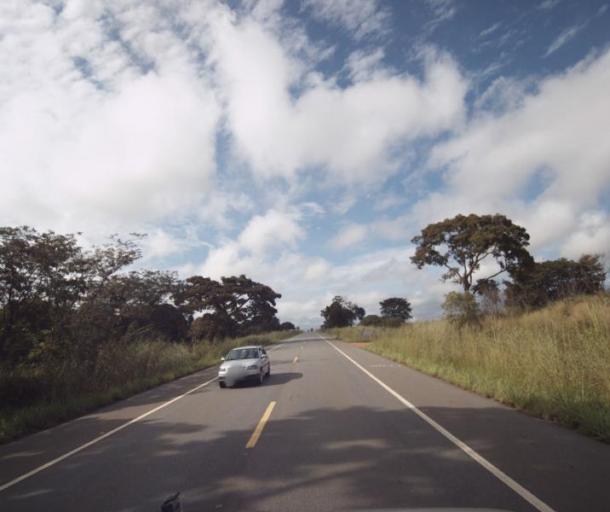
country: BR
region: Goias
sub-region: Barro Alto
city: Barro Alto
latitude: -15.2452
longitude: -48.6901
